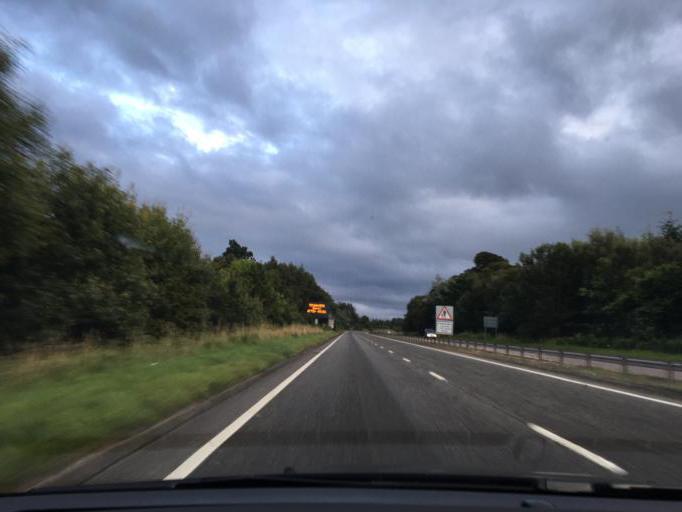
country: GB
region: Scotland
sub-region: Highland
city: Inverness
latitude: 57.4655
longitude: -4.1750
